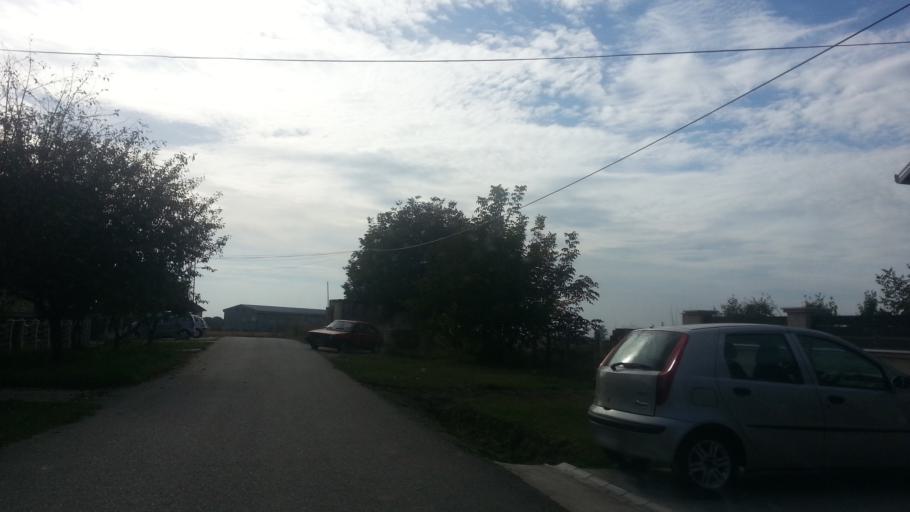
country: RS
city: Belegis
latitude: 45.0121
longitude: 20.3162
